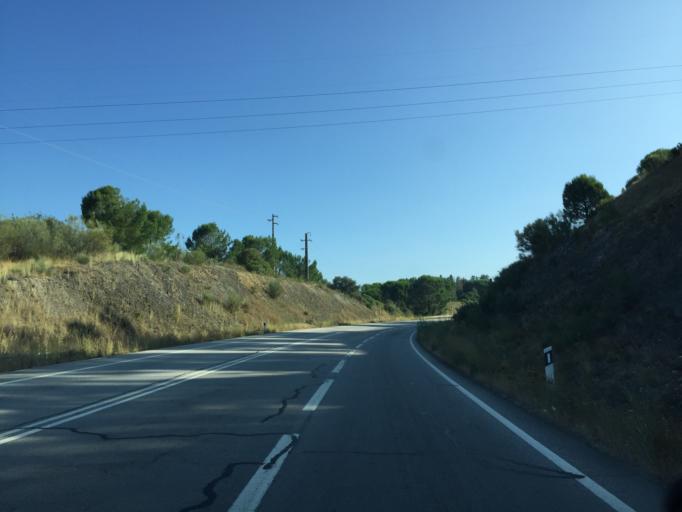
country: PT
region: Santarem
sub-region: Abrantes
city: Alferrarede
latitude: 39.4945
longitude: -8.1748
